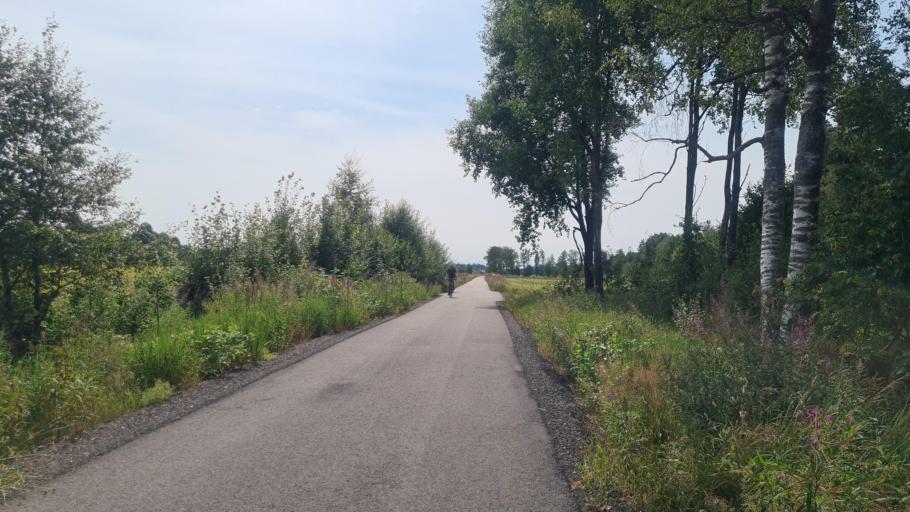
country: SE
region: Kronoberg
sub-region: Ljungby Kommun
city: Lagan
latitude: 56.8856
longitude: 13.9844
